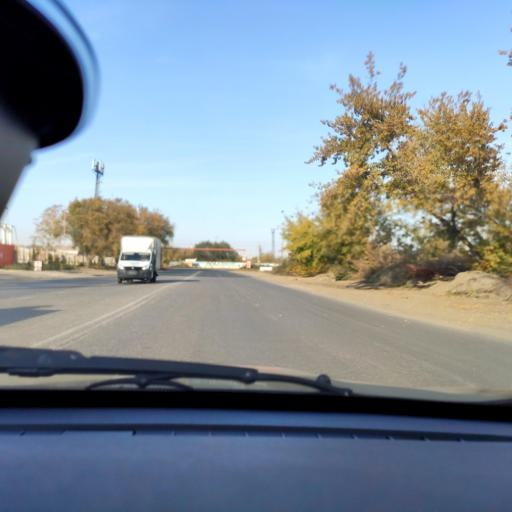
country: RU
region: Samara
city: Tol'yatti
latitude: 53.5271
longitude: 49.4724
